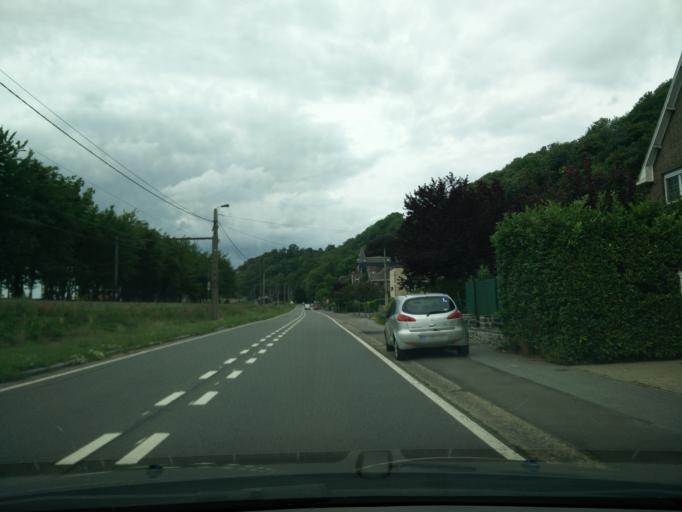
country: BE
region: Wallonia
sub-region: Province de Liege
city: Vise
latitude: 50.7157
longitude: 5.6889
